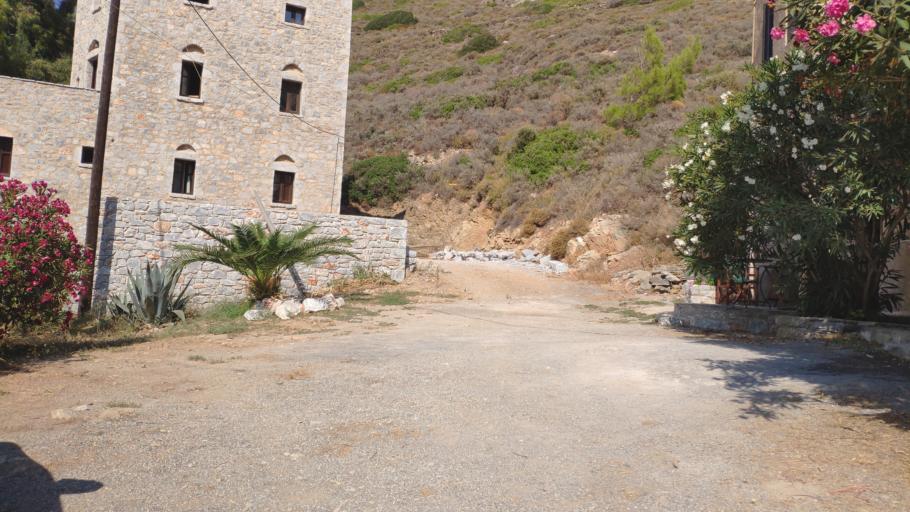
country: GR
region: Peloponnese
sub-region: Nomos Lakonias
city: Gytheio
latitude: 36.4279
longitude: 22.4872
